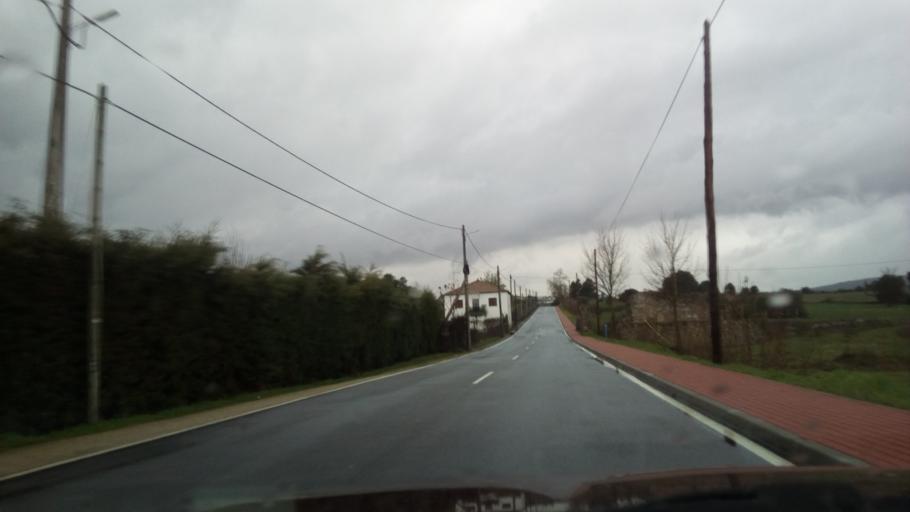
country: PT
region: Guarda
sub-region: Celorico da Beira
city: Celorico da Beira
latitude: 40.6395
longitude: -7.3627
